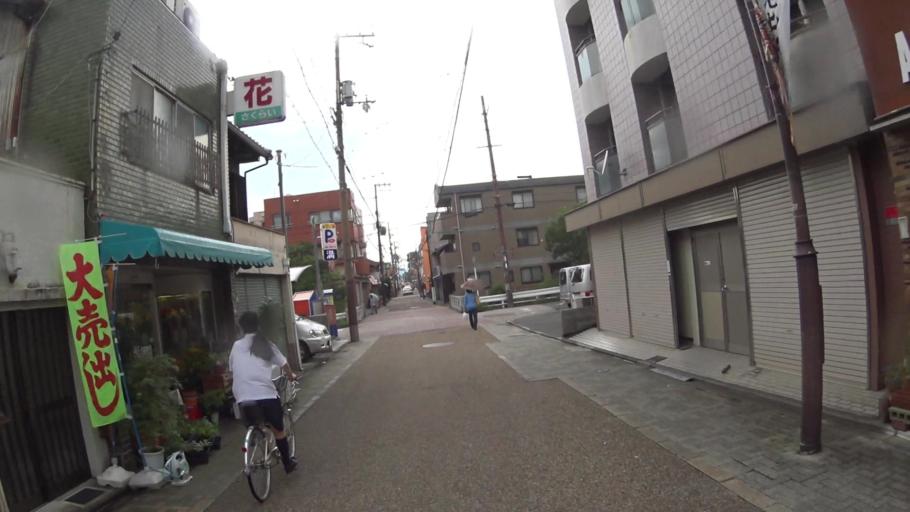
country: JP
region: Kyoto
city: Kyoto
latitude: 35.0262
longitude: 135.7333
